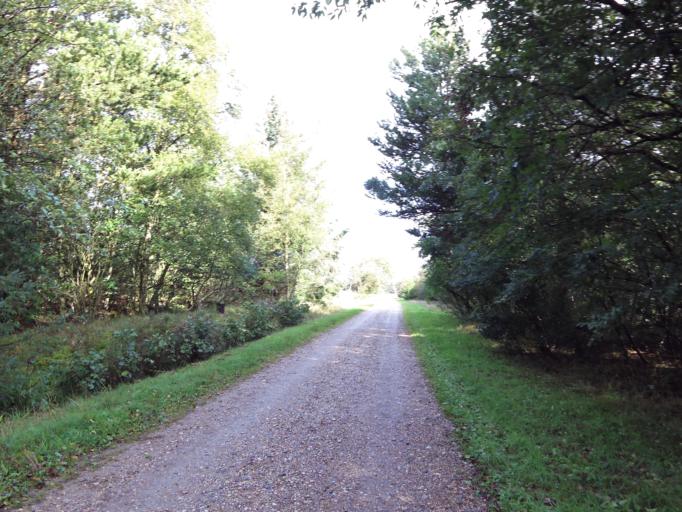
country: DK
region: South Denmark
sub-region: Varde Kommune
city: Oksbol
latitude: 55.5585
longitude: 8.2108
